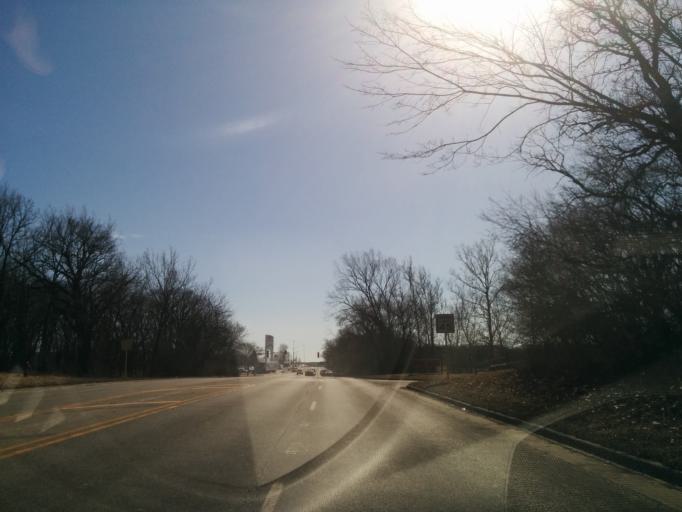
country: US
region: Illinois
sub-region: Cook County
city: Hodgkins
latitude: 41.7705
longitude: -87.8680
